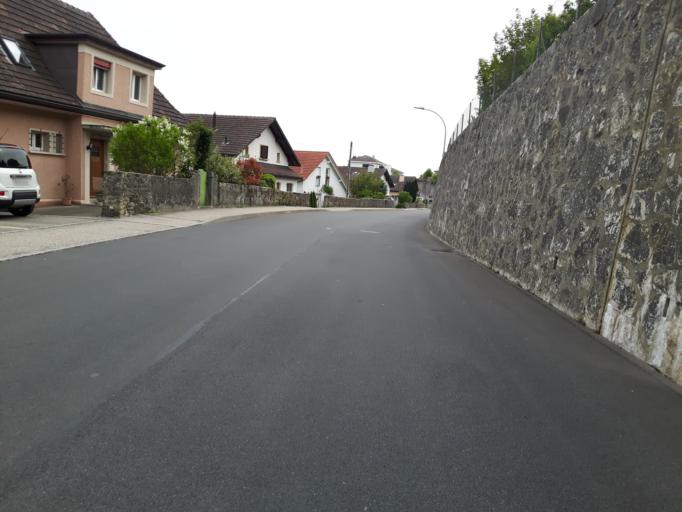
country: CH
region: Neuchatel
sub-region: Boudry District
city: Gorgier
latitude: 46.9012
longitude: 6.7796
